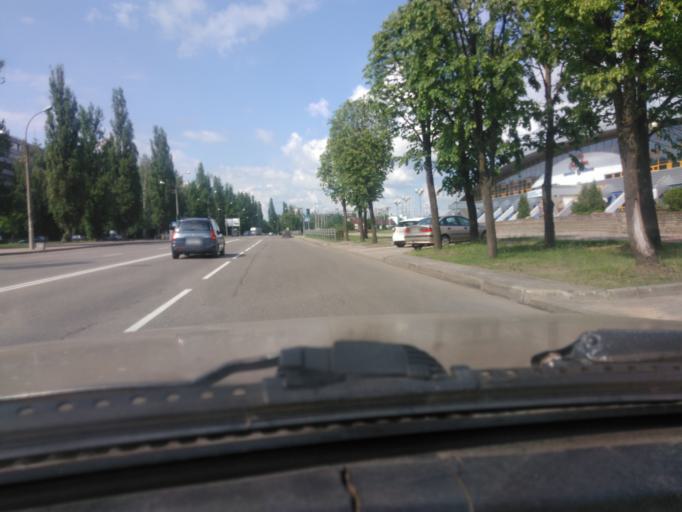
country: BY
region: Mogilev
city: Mahilyow
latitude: 53.9276
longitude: 30.3620
